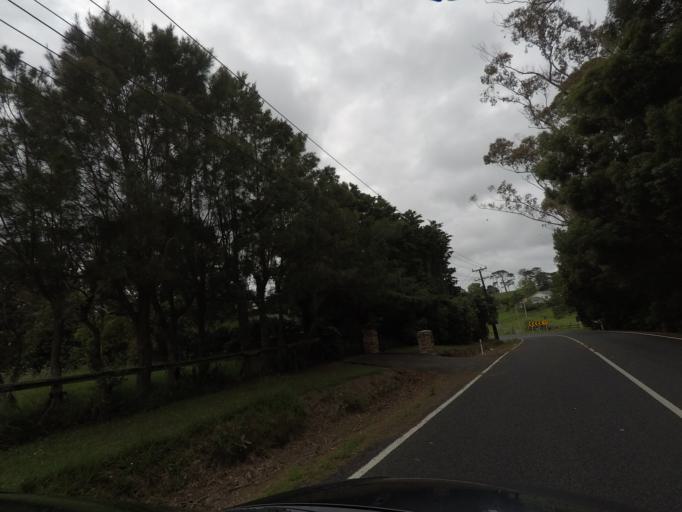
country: NZ
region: Auckland
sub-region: Auckland
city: Rosebank
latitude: -36.8207
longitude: 174.5701
